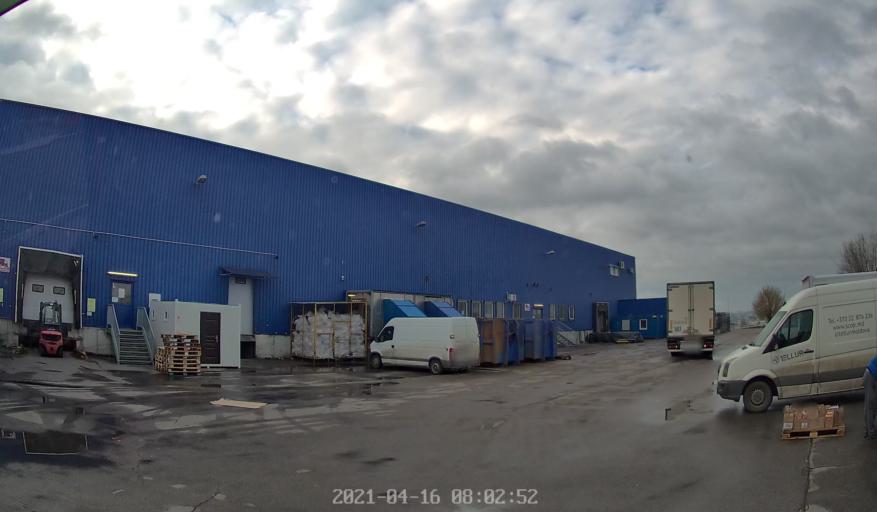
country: MD
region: Chisinau
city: Stauceni
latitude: 47.0654
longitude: 28.8528
